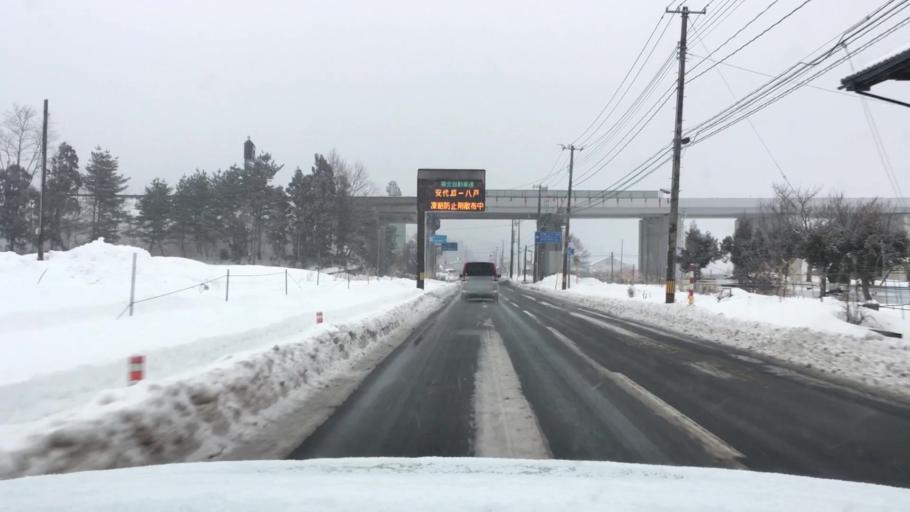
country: JP
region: Iwate
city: Ichinohe
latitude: 40.1080
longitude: 141.0512
